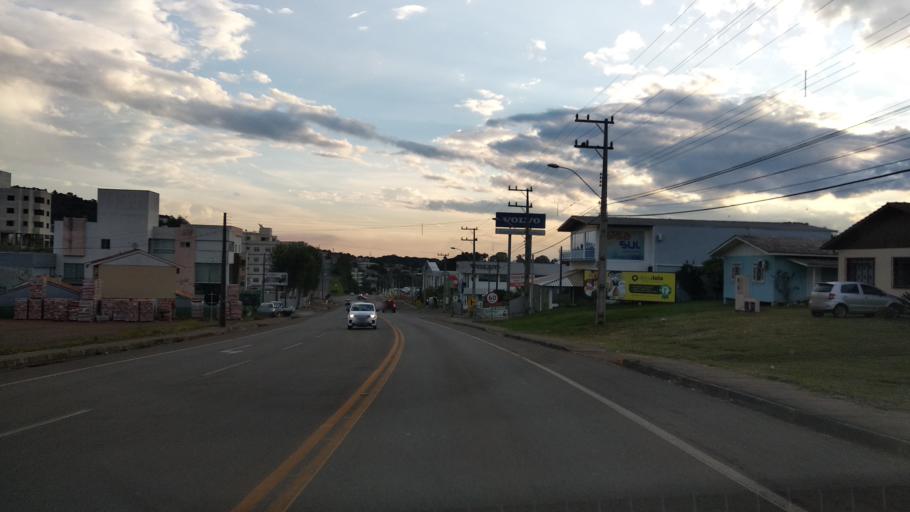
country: BR
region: Santa Catarina
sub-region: Videira
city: Videira
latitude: -26.9989
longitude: -51.1188
